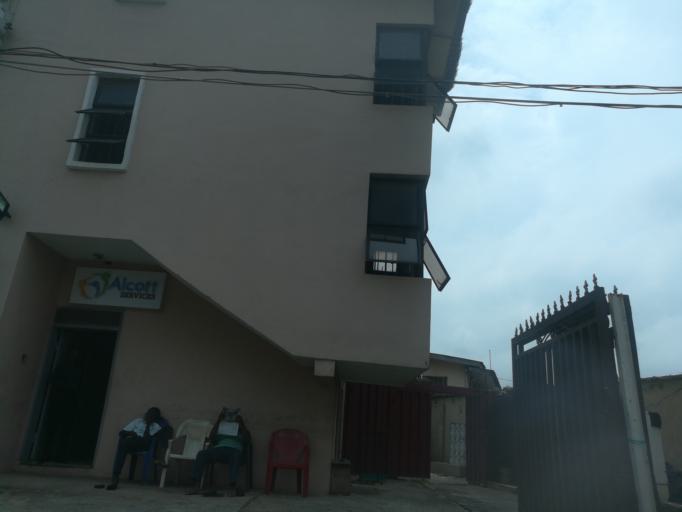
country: NG
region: Lagos
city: Ojota
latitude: 6.5726
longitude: 3.3624
